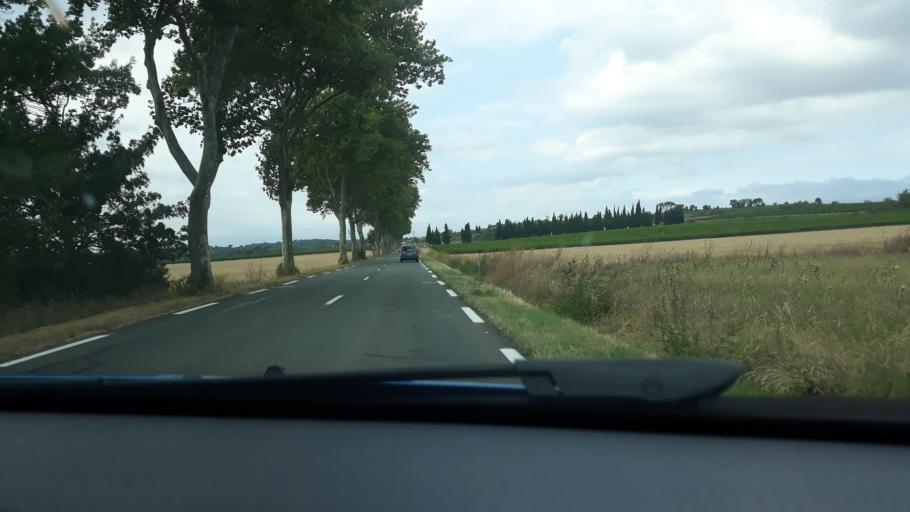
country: FR
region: Languedoc-Roussillon
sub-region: Departement de l'Aude
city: Pezens
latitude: 43.2669
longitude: 2.2406
